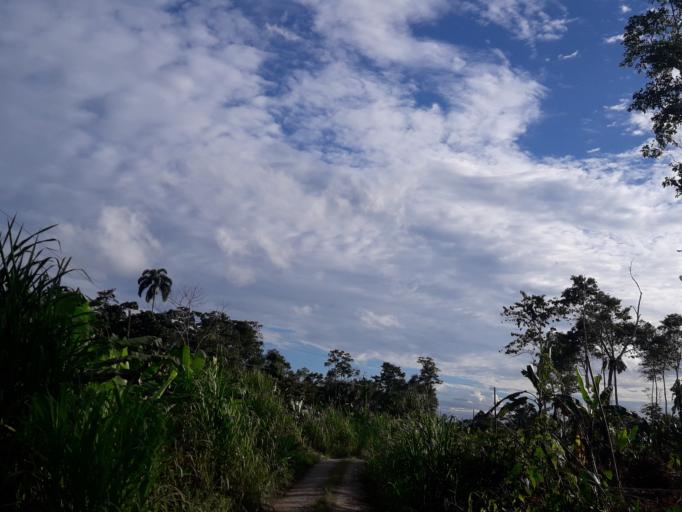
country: EC
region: Orellana
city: Boca Suno
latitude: -0.8867
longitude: -77.3002
